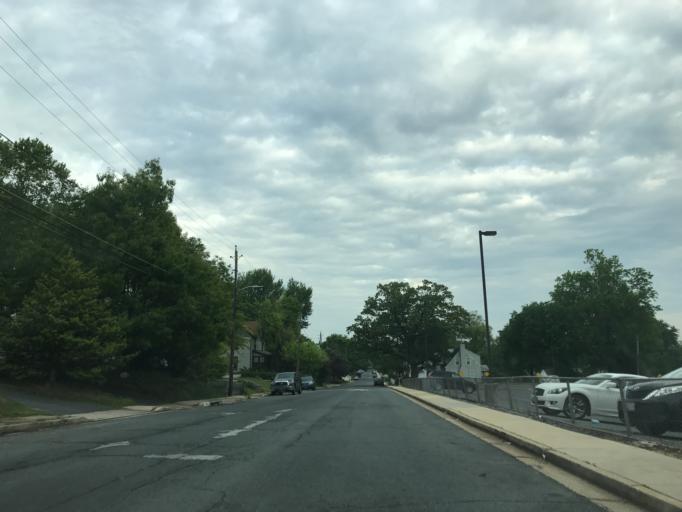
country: US
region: Maryland
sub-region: Baltimore County
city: Parkville
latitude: 39.3819
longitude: -76.5346
